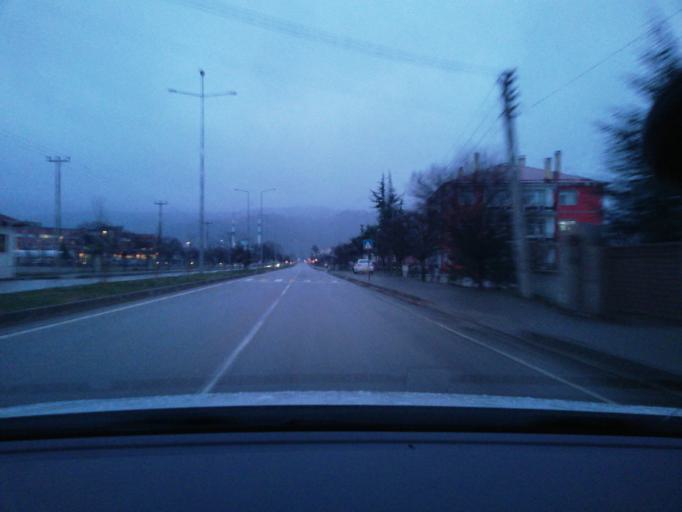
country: TR
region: Bolu
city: Bolu
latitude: 40.6939
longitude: 31.6194
